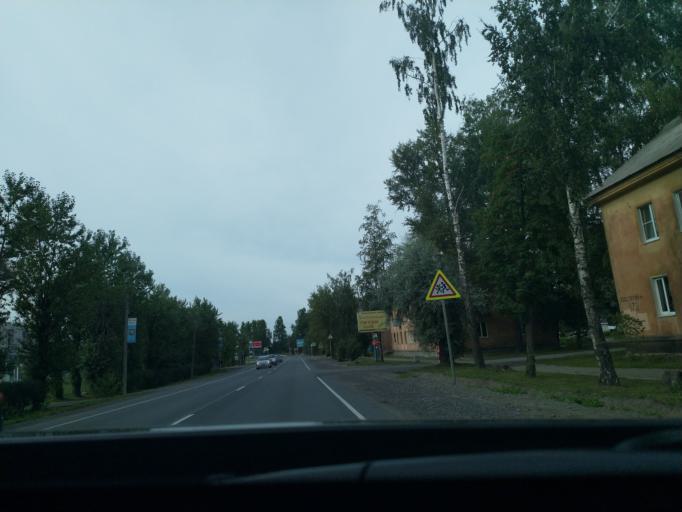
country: RU
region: Leningrad
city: Nikol'skoye
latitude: 59.7059
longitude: 30.7844
